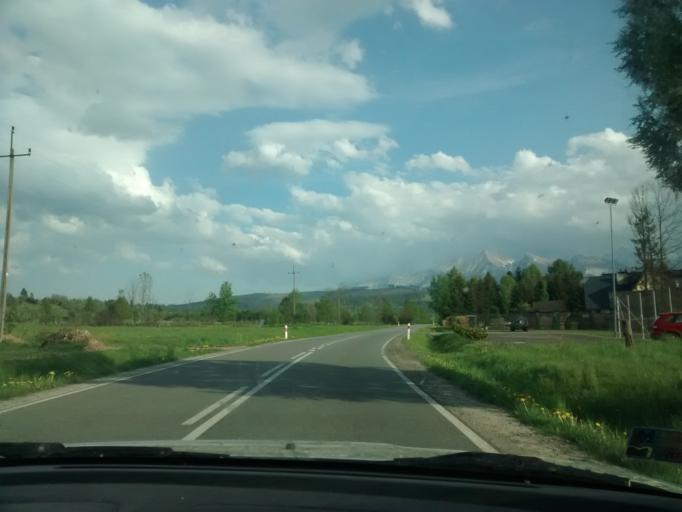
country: PL
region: Lesser Poland Voivodeship
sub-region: Powiat tatrzanski
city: Bukowina Tatrzanska
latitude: 49.3393
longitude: 20.1435
